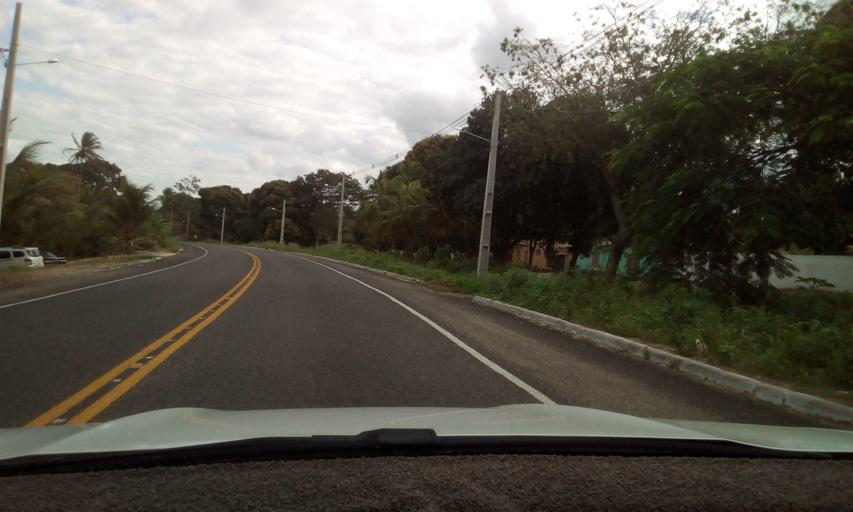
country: BR
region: Paraiba
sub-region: Mamanguape
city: Mamanguape
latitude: -6.8222
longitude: -35.1074
